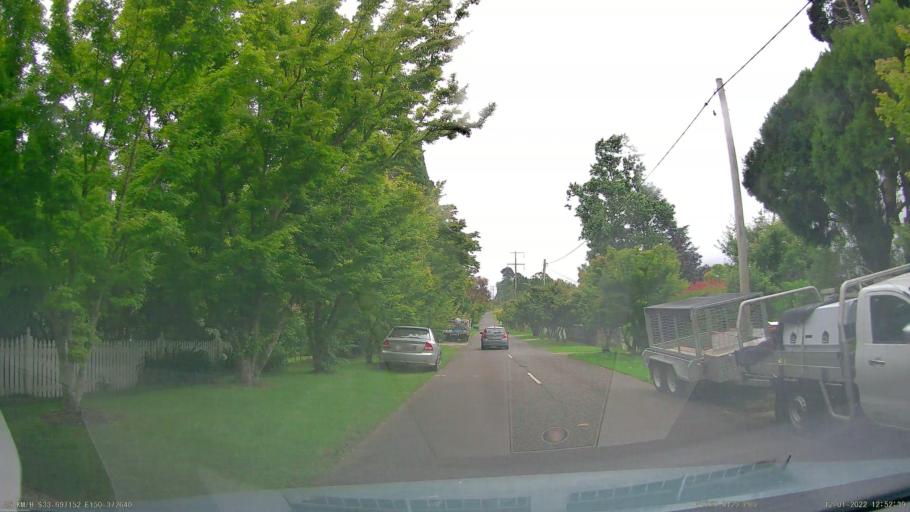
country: AU
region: New South Wales
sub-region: Blue Mountains Municipality
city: Leura
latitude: -33.6970
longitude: 150.3725
